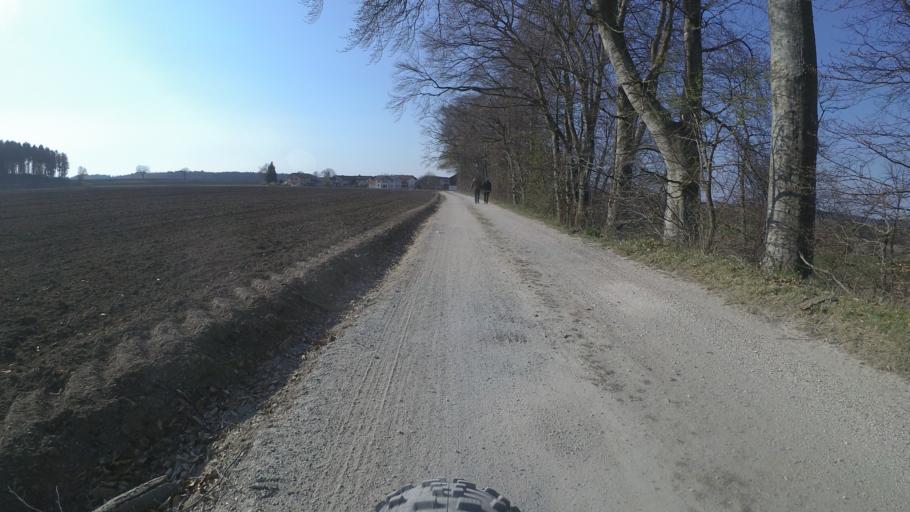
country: DE
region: Bavaria
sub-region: Upper Bavaria
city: Nussdorf
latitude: 47.9268
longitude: 12.6064
